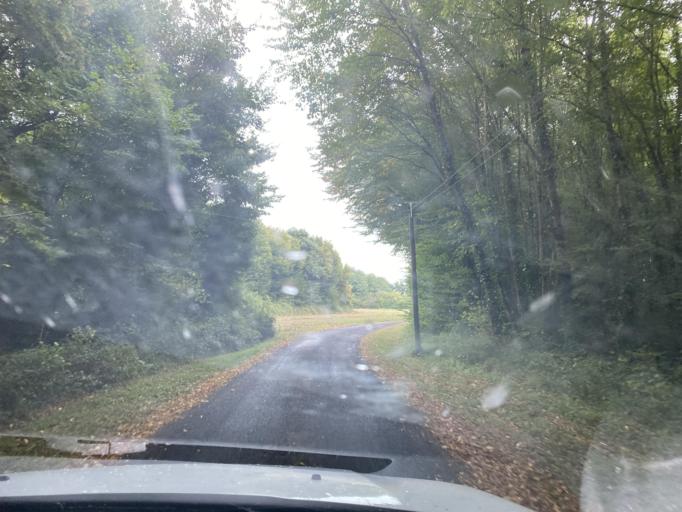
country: FR
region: Poitou-Charentes
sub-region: Departement de la Charente-Maritime
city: Gemozac
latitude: 45.5415
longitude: -0.6466
